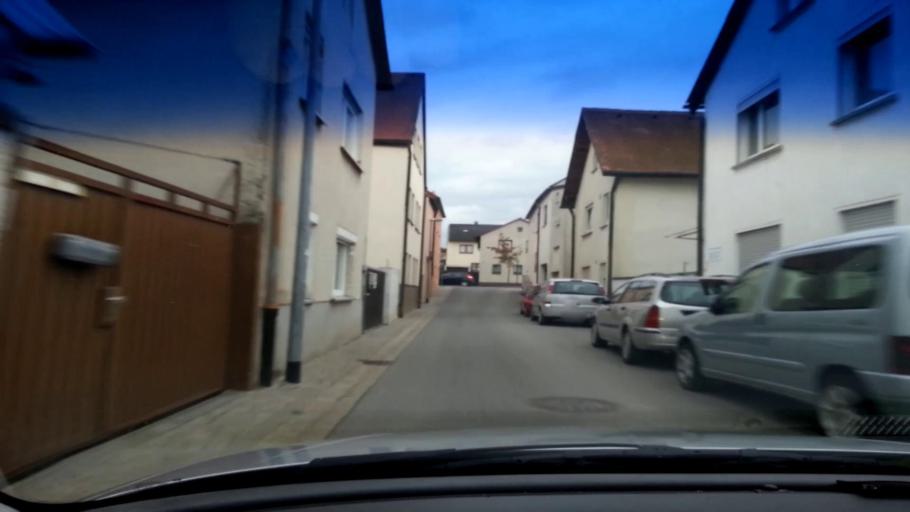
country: DE
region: Bavaria
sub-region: Upper Franconia
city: Hallstadt
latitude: 49.9263
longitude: 10.8741
